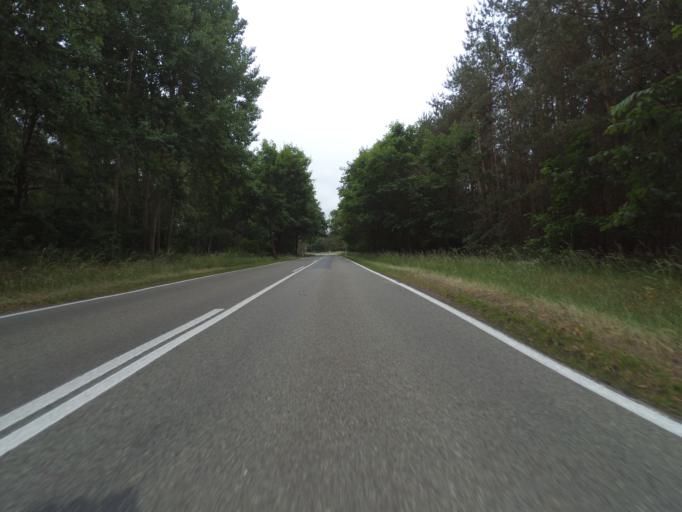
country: DE
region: Mecklenburg-Vorpommern
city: Neustadt-Glewe
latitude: 53.3729
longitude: 11.6439
